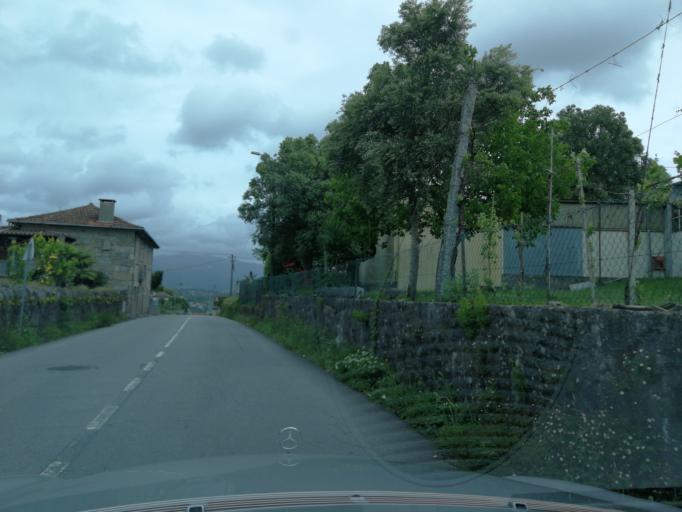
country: PT
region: Braga
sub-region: Amares
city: Amares
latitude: 41.6060
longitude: -8.3557
